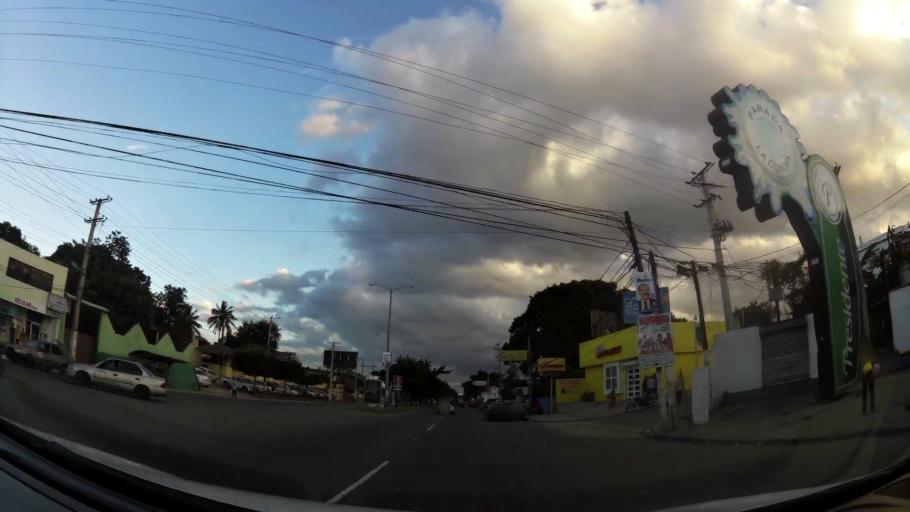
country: DO
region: Santiago
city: Licey al Medio
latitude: 19.4103
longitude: -70.6404
